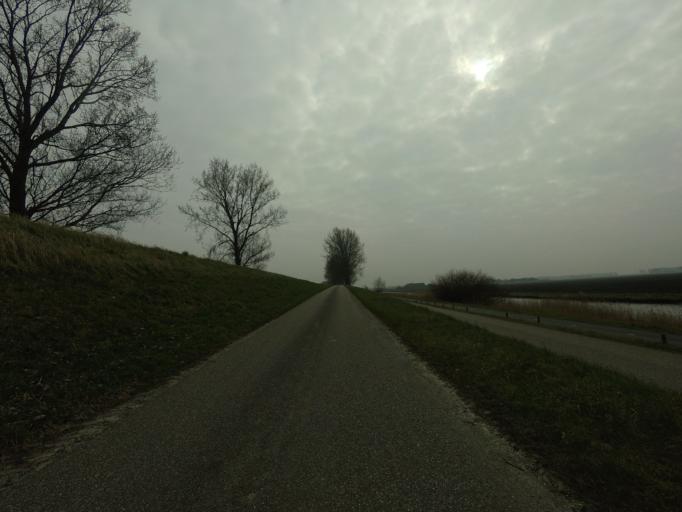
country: NL
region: Zeeland
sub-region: Gemeente Hulst
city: Hulst
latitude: 51.3472
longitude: 4.1082
